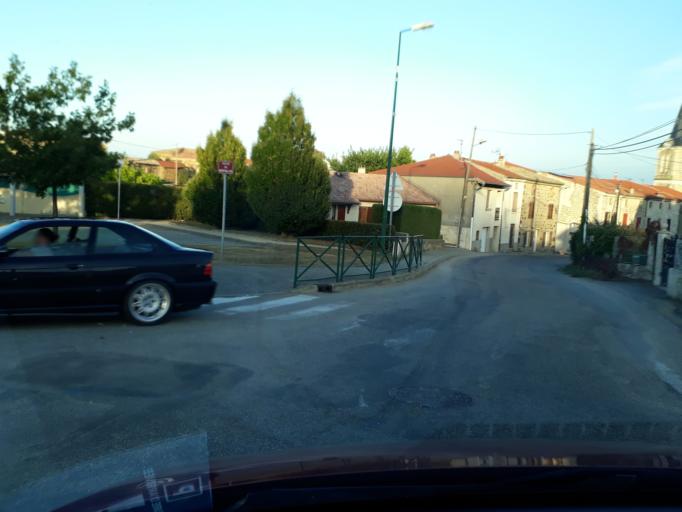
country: FR
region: Rhone-Alpes
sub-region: Departement de l'Ardeche
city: Felines
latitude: 45.3173
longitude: 4.7260
